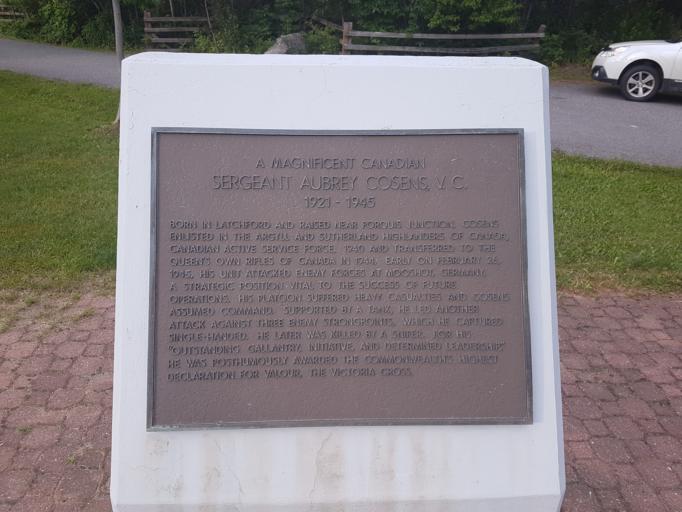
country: CA
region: Ontario
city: Temiskaming Shores
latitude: 47.3235
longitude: -79.8101
